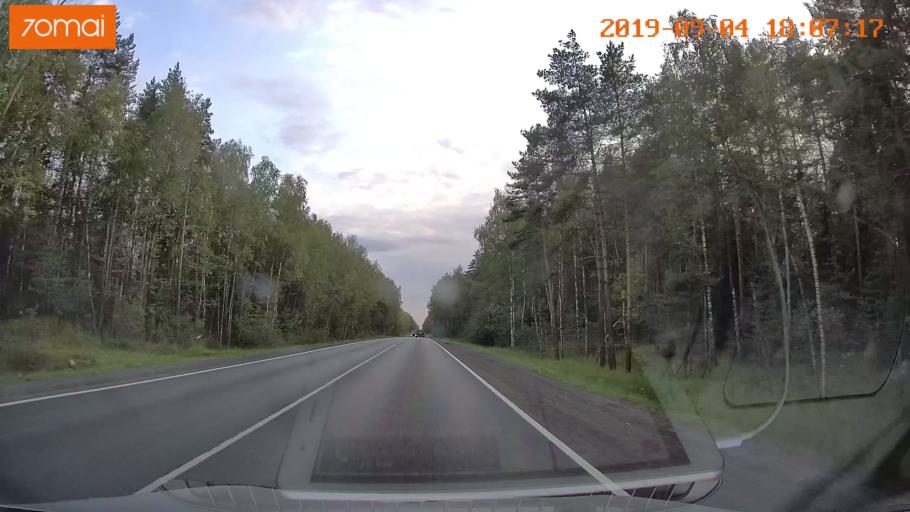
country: RU
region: Moskovskaya
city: Khorlovo
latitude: 55.4209
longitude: 38.8030
